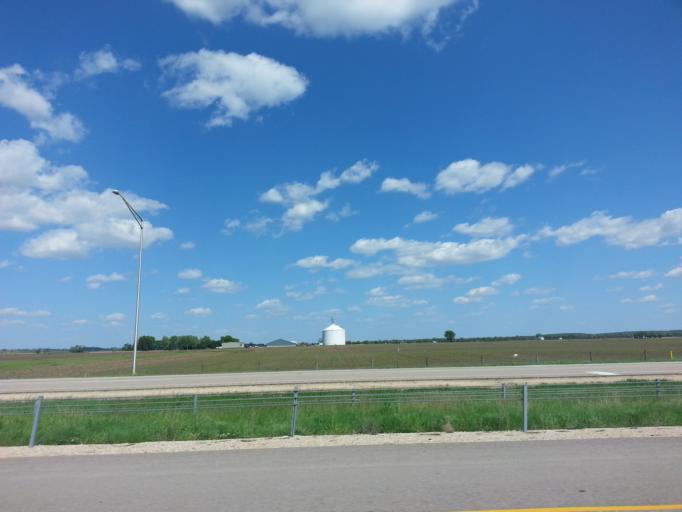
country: US
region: Wisconsin
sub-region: Rock County
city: Beloit
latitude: 42.5908
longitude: -88.9819
